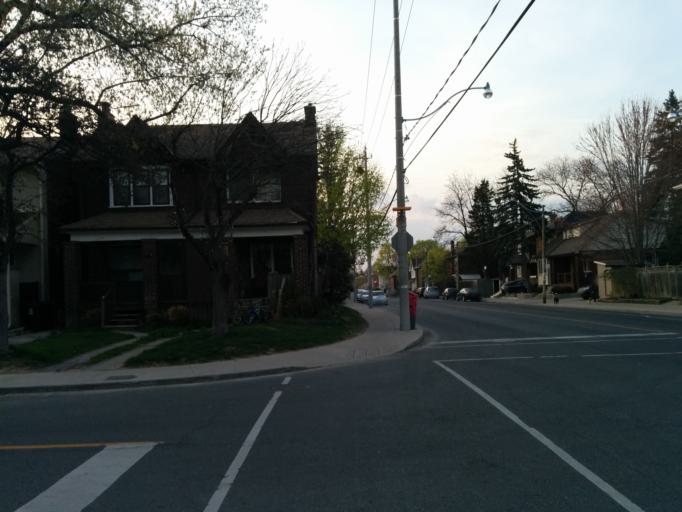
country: CA
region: Ontario
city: Toronto
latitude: 43.7284
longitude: -79.3976
